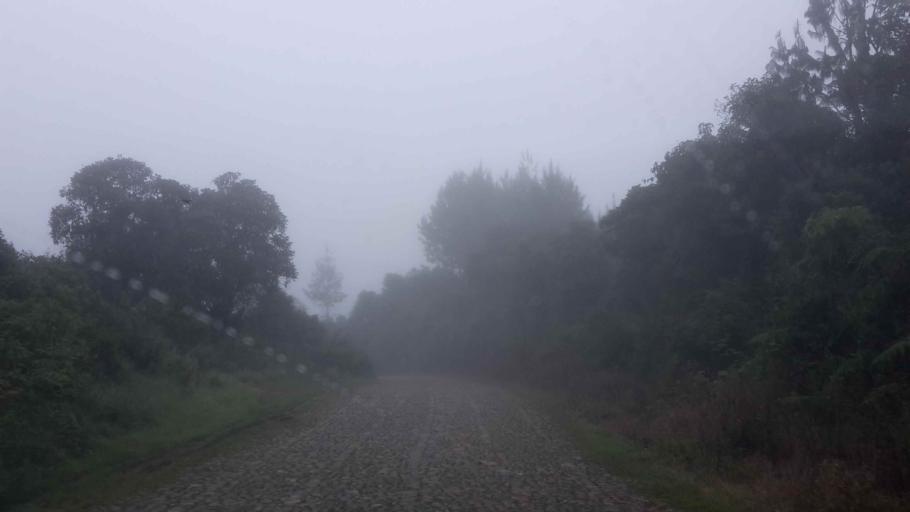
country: BO
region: Cochabamba
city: Colomi
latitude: -17.1215
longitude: -65.9627
